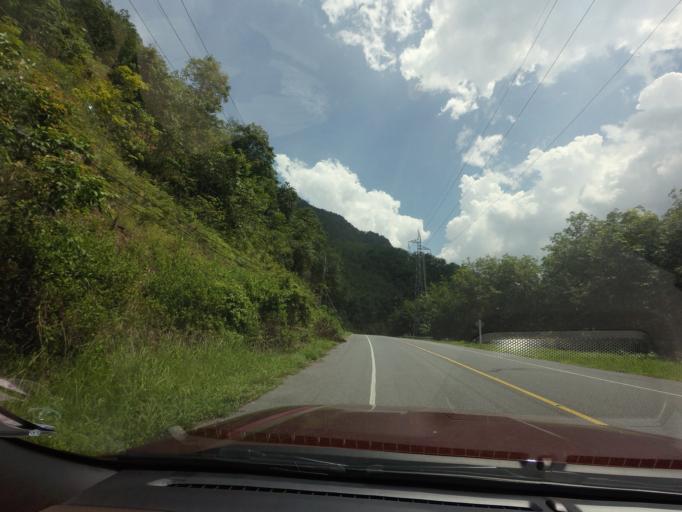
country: TH
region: Yala
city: Than To
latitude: 5.9946
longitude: 101.1919
